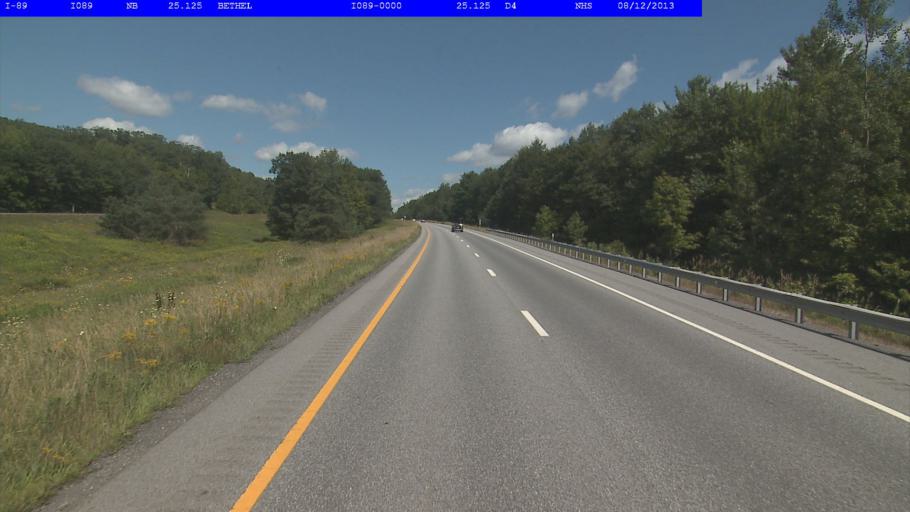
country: US
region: Vermont
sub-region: Orange County
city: Randolph
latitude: 43.8631
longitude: -72.6074
